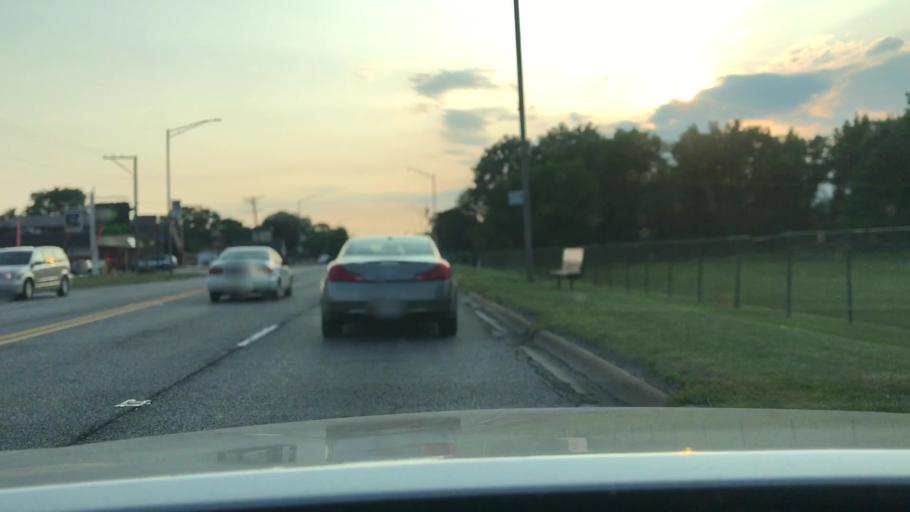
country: US
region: Illinois
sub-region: Cook County
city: Justice
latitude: 41.7475
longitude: -87.8317
